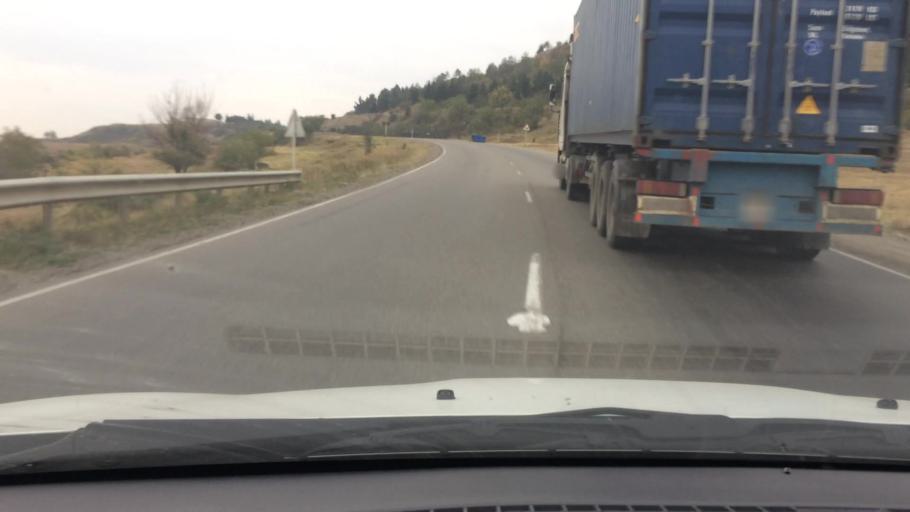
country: GE
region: T'bilisi
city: Tbilisi
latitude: 41.6007
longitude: 44.7785
